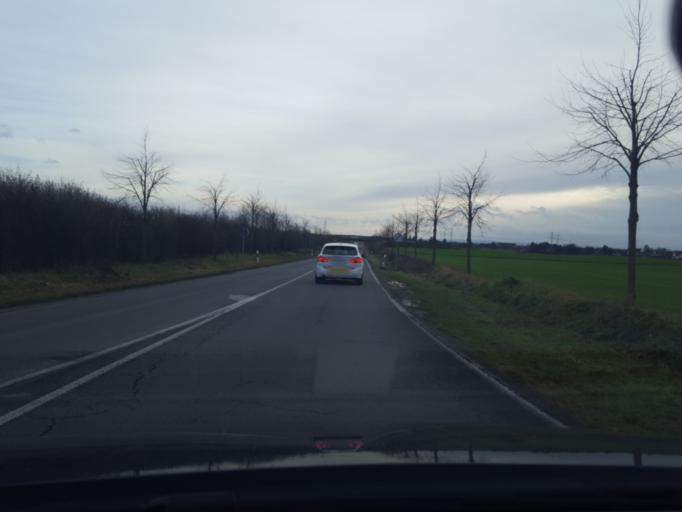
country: DE
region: North Rhine-Westphalia
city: Niederkassel
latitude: 50.8256
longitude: 7.0443
